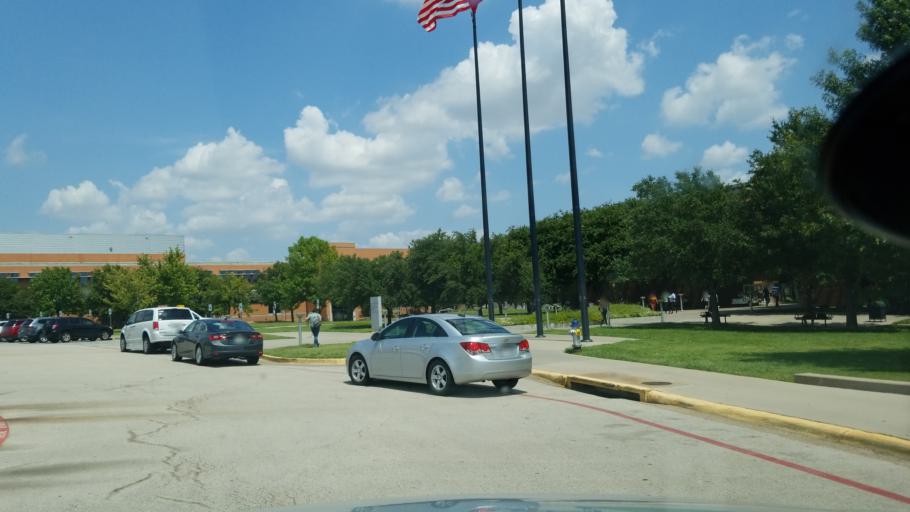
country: US
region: Texas
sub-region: Dallas County
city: Richardson
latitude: 32.9203
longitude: -96.7316
